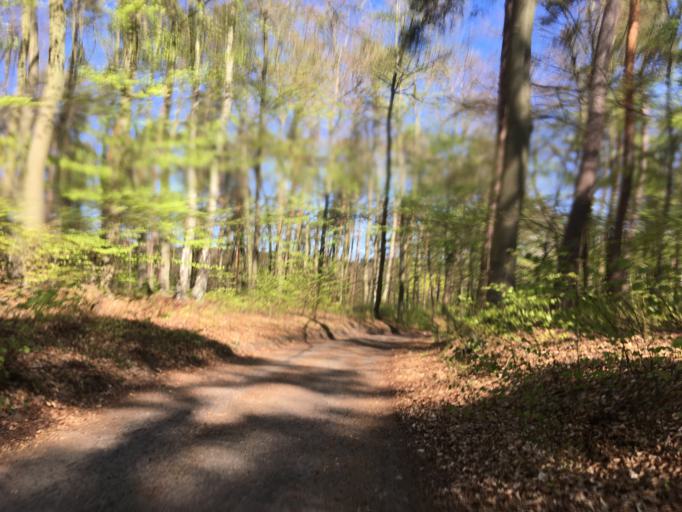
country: DE
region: Brandenburg
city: Wandlitz
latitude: 52.7543
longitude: 13.5338
